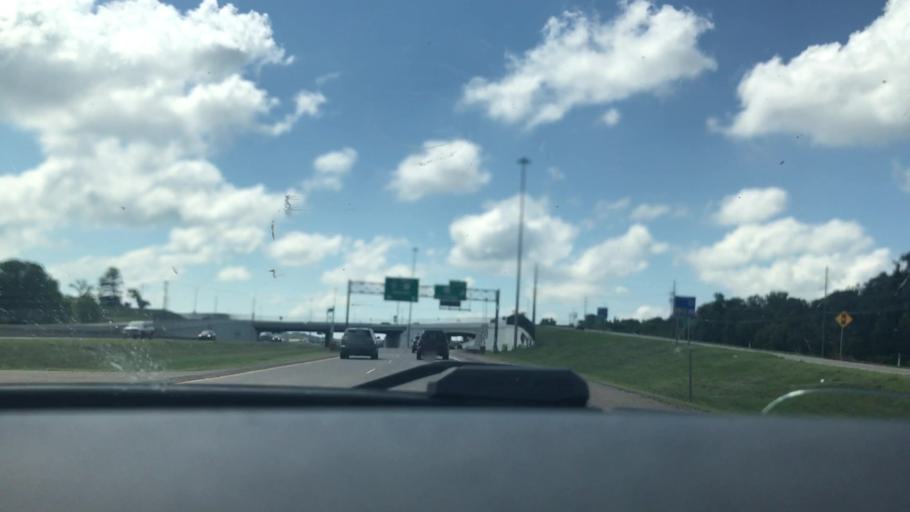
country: US
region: Wisconsin
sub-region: Eau Claire County
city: Altoona
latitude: 44.7983
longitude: -91.4562
